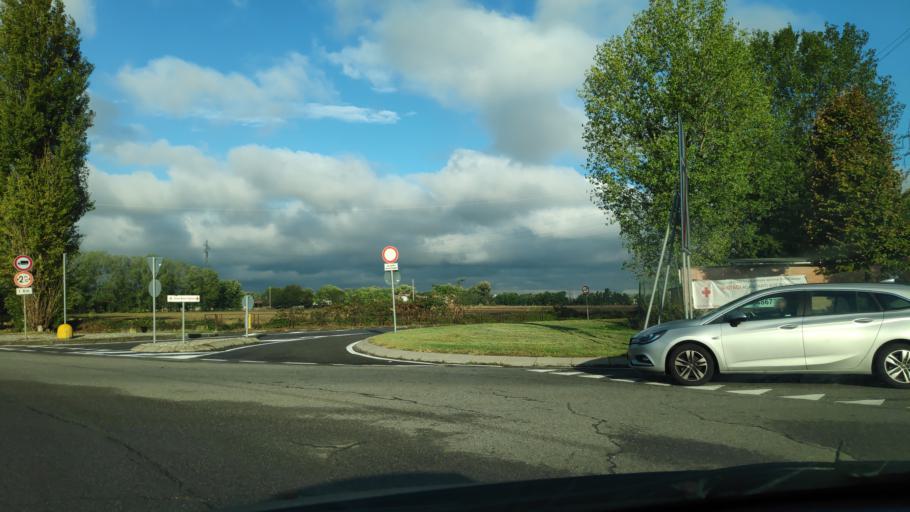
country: IT
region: Lombardy
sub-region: Citta metropolitana di Milano
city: Opera
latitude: 45.3829
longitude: 9.2135
